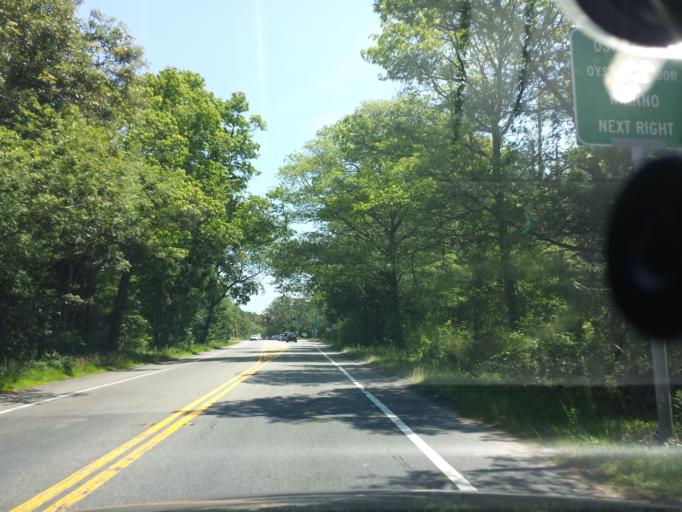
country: US
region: Massachusetts
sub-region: Barnstable County
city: Marstons Mills
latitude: 41.6520
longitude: -70.4066
